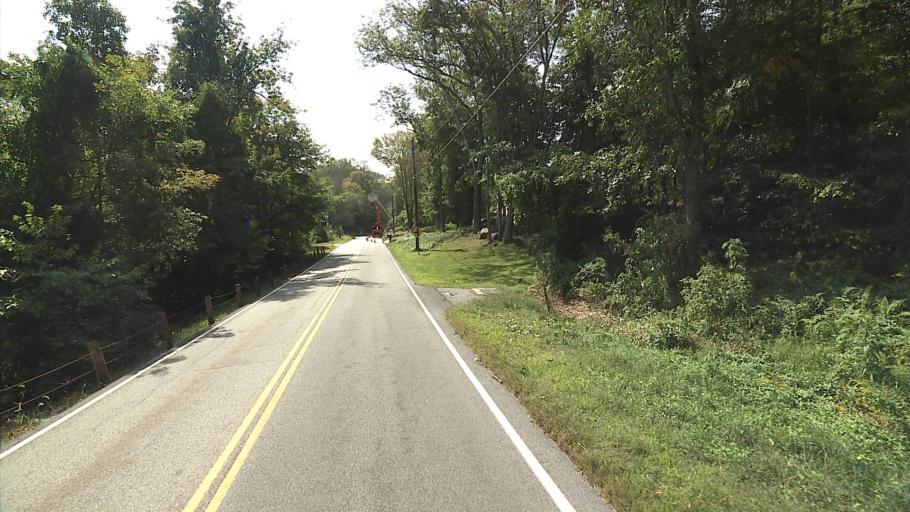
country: US
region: Connecticut
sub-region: Windham County
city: Wauregan
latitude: 41.7445
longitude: -71.9597
